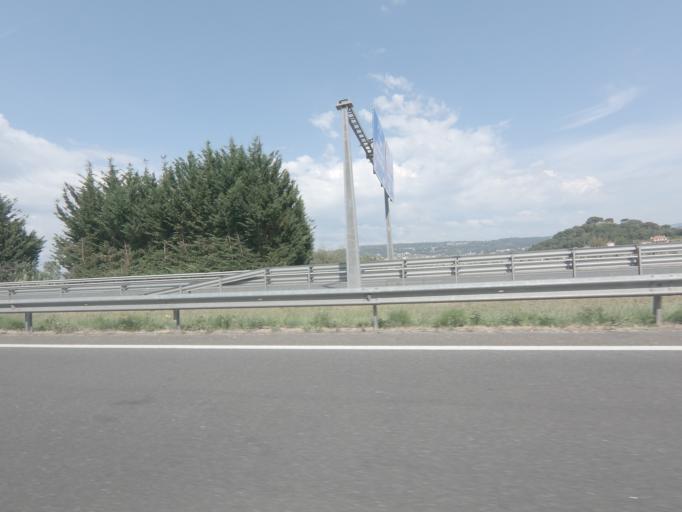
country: ES
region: Galicia
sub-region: Provincia de Ourense
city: Ourense
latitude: 42.3346
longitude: -7.8864
